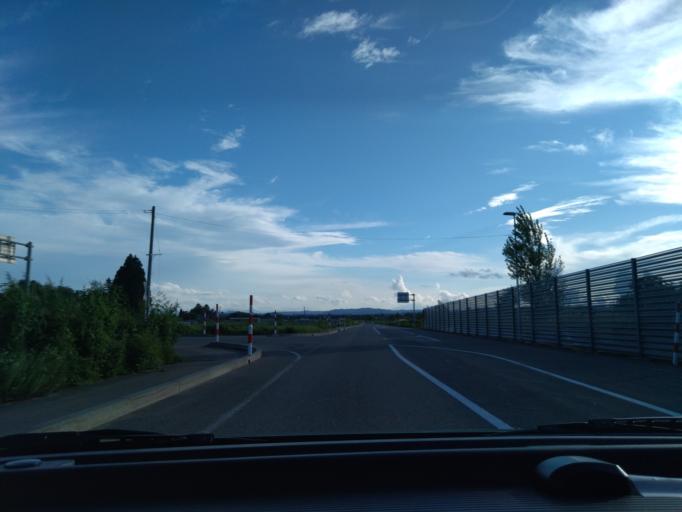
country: JP
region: Akita
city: Omagari
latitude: 39.4112
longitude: 140.4810
